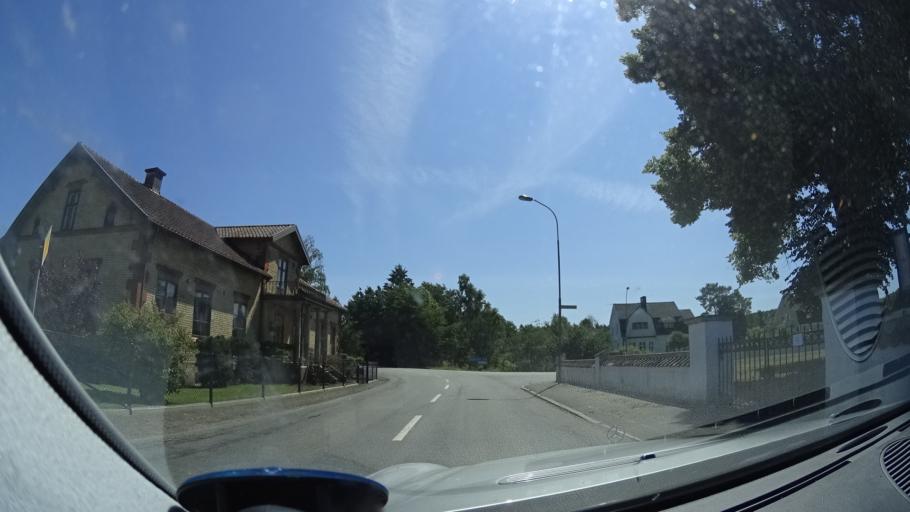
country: SE
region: Skane
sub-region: Kristianstads Kommun
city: Degeberga
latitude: 55.8851
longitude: 14.0180
